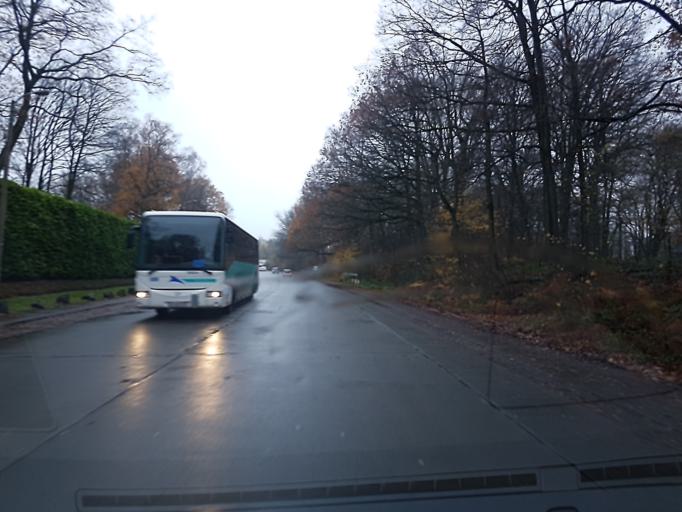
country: BE
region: Wallonia
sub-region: Province de Liege
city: Esneux
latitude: 50.5793
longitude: 5.5559
